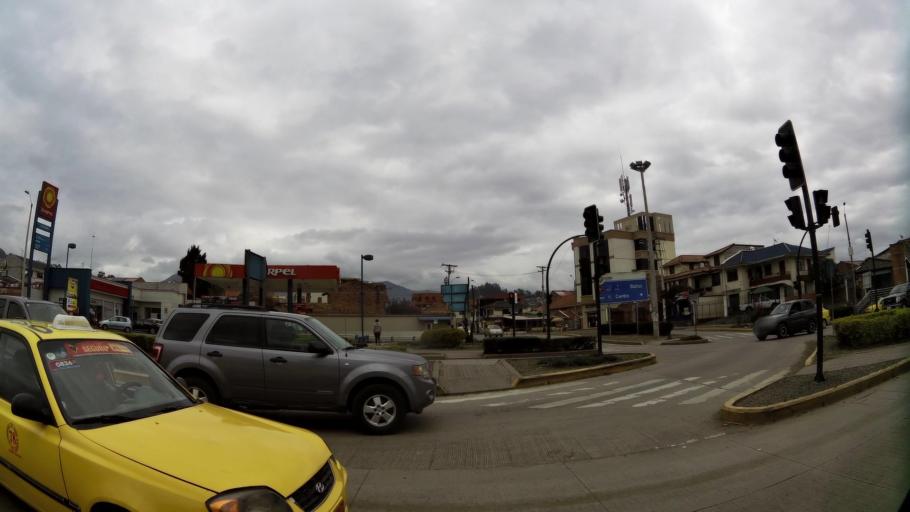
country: EC
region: Azuay
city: Cuenca
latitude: -2.9240
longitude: -79.0396
